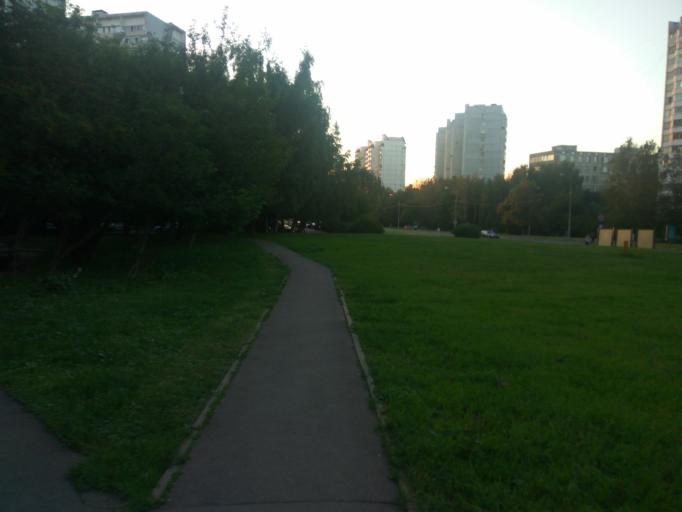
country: RU
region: Moscow
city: Tyoply Stan
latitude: 55.6353
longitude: 37.5147
